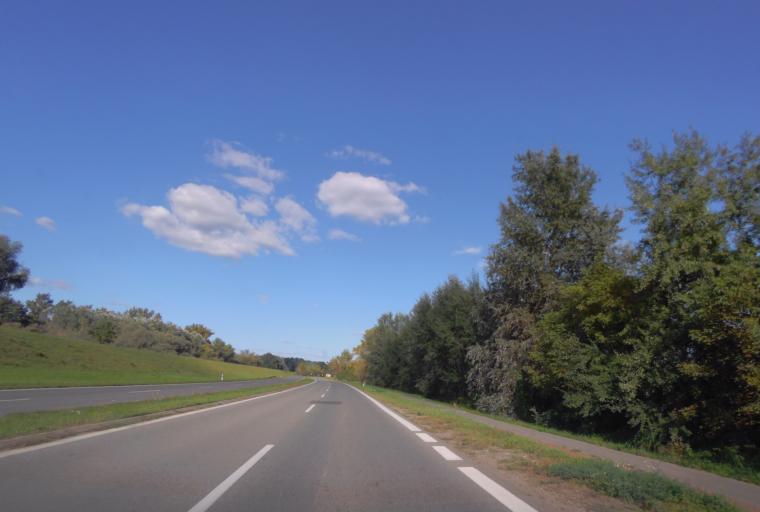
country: PL
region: Subcarpathian Voivodeship
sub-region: Tarnobrzeg
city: Tarnobrzeg
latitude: 50.5595
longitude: 21.6499
